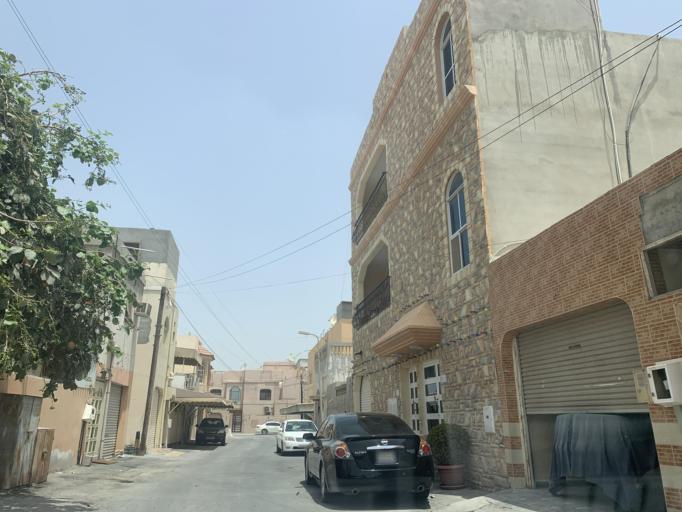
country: BH
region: Northern
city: Madinat `Isa
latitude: 26.1545
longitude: 50.5245
